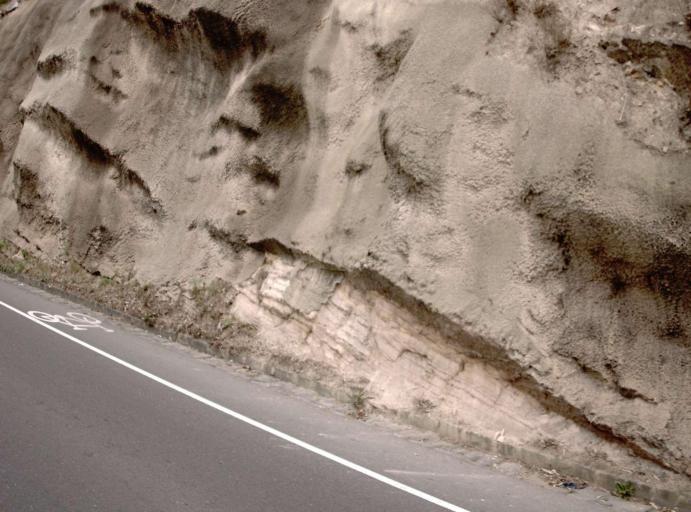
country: AU
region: Victoria
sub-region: Manningham
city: Bulleen
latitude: -37.7689
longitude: 145.0653
